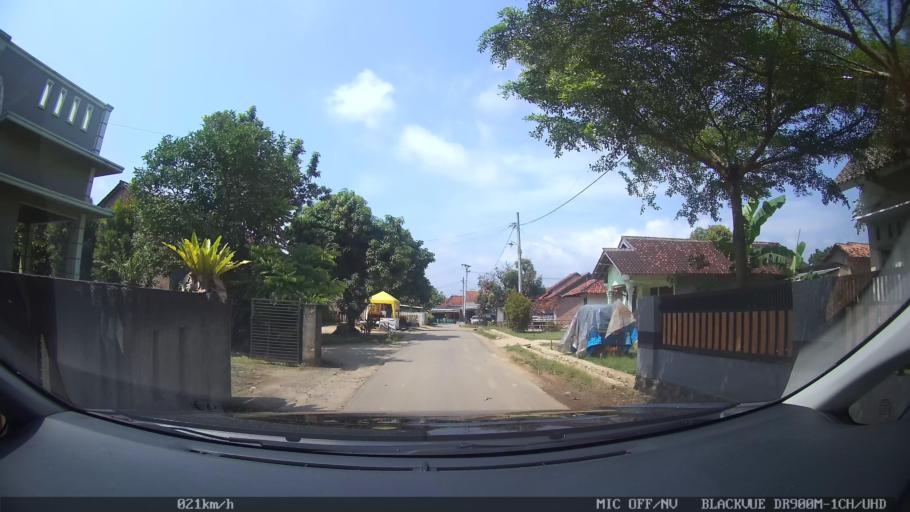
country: ID
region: Lampung
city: Kedaton
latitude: -5.3405
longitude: 105.2714
